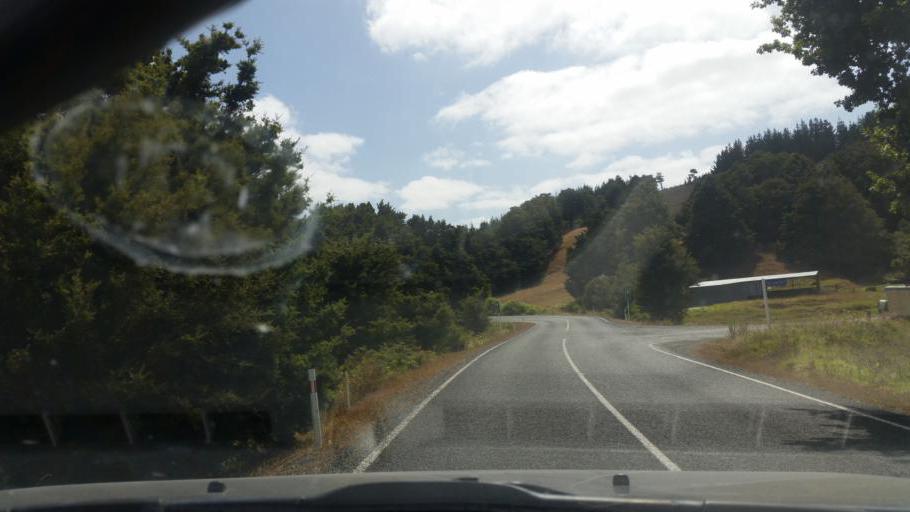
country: NZ
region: Northland
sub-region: Whangarei
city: Ruakaka
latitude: -35.9427
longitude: 174.2919
